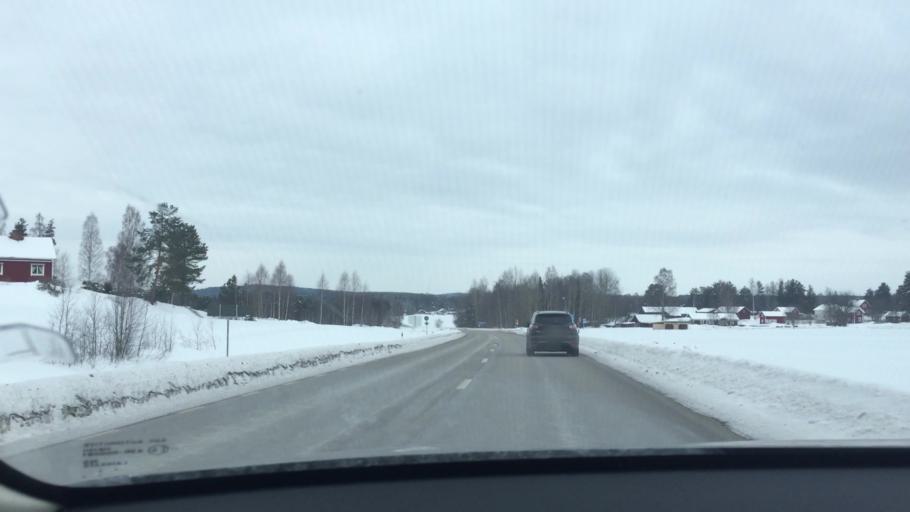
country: SE
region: Dalarna
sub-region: Faluns Kommun
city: Svardsjo
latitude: 60.6421
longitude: 15.8410
